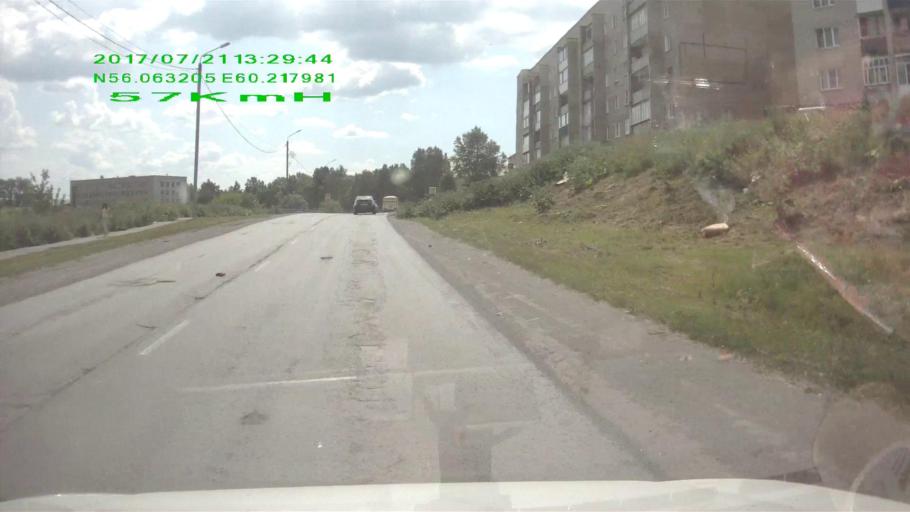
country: RU
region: Chelyabinsk
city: Verkhniy Ufaley
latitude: 56.0621
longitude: 60.2180
